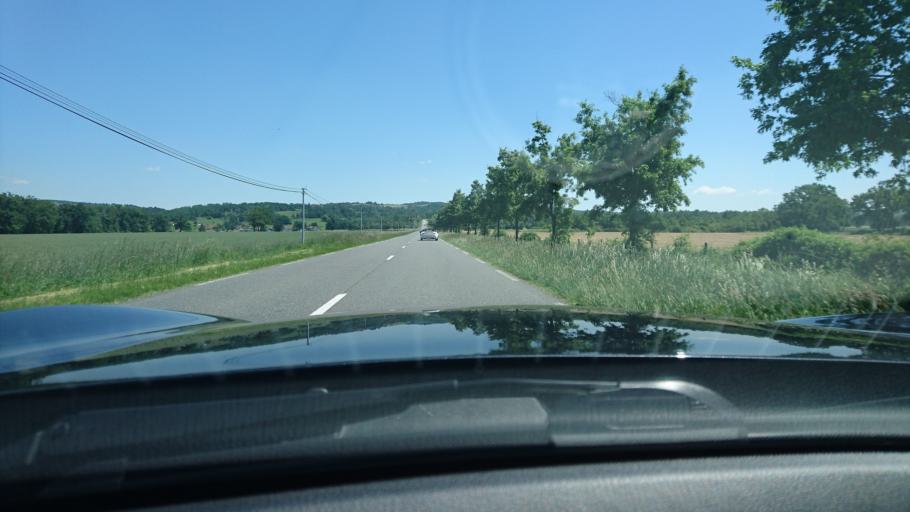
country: FR
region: Rhone-Alpes
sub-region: Departement de la Loire
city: Feurs
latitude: 45.7356
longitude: 4.2730
